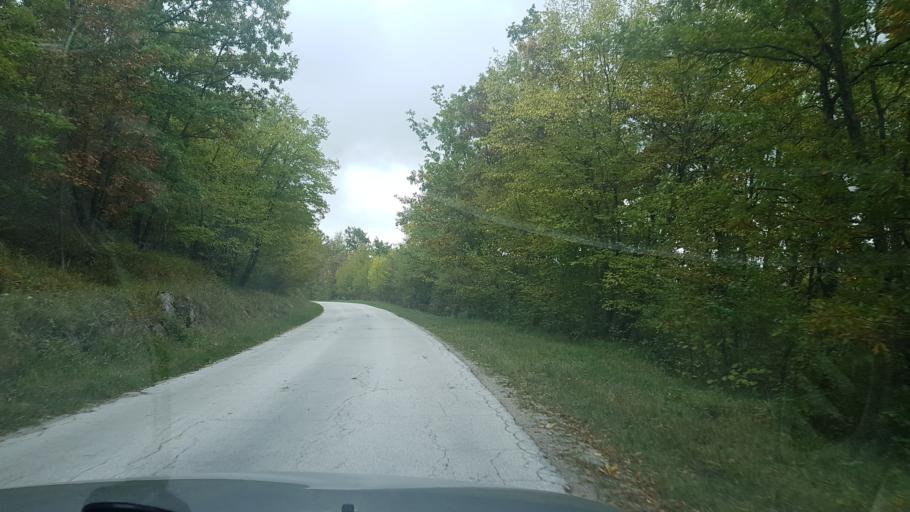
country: HR
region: Istarska
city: Buzet
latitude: 45.5048
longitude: 13.9805
